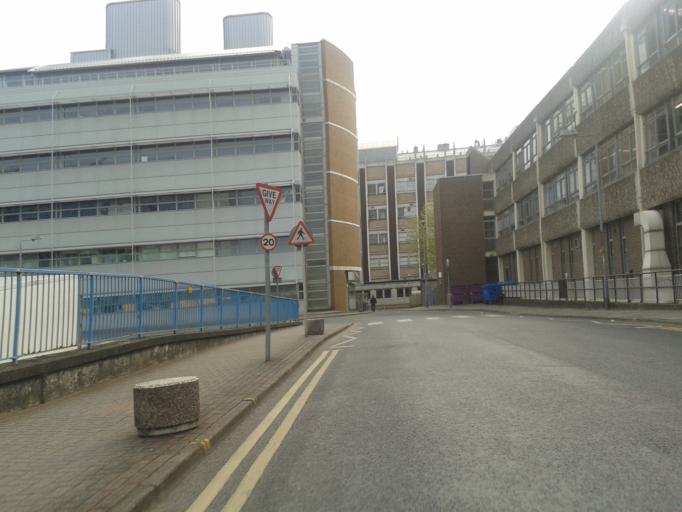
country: GB
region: England
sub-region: Cambridgeshire
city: Cambridge
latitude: 52.1760
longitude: 0.1410
